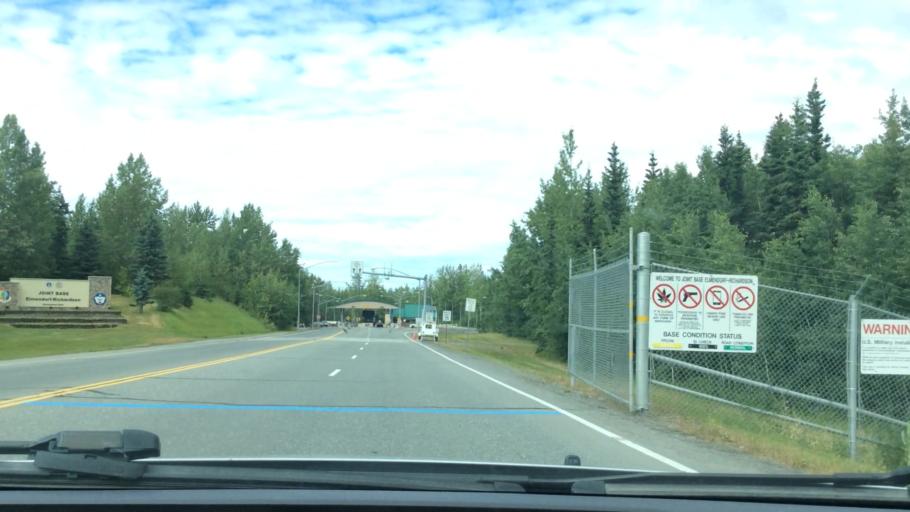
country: US
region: Alaska
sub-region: Anchorage Municipality
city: Elmendorf Air Force Base
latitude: 61.2550
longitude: -149.6613
